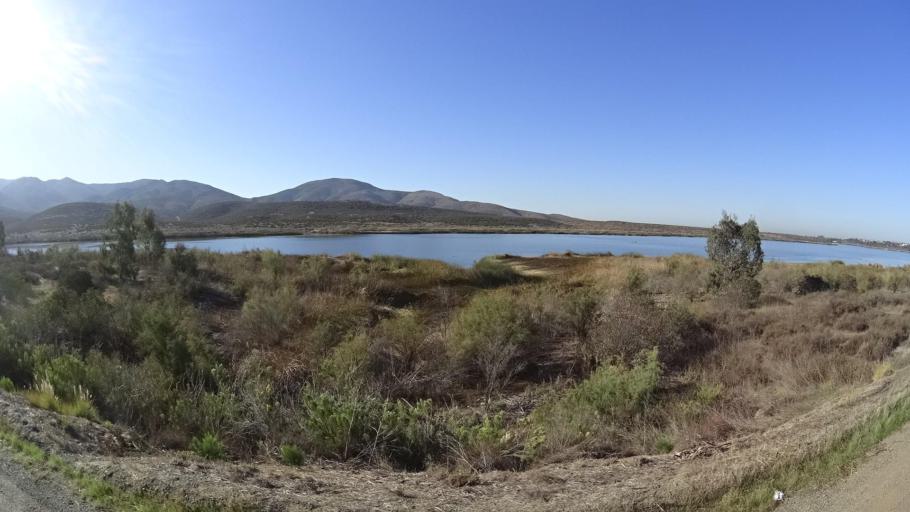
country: US
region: California
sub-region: San Diego County
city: Jamul
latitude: 32.6345
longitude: -116.9073
